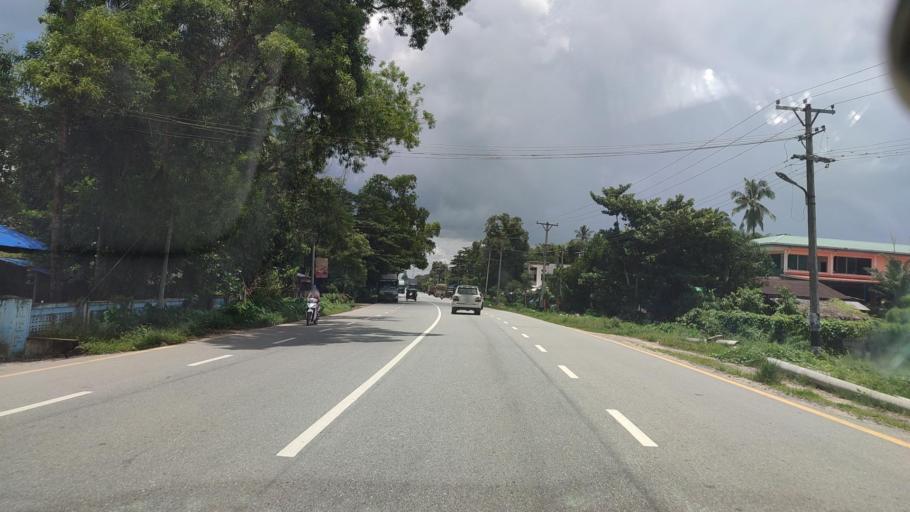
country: MM
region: Bago
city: Pyu
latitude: 18.4925
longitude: 96.4368
